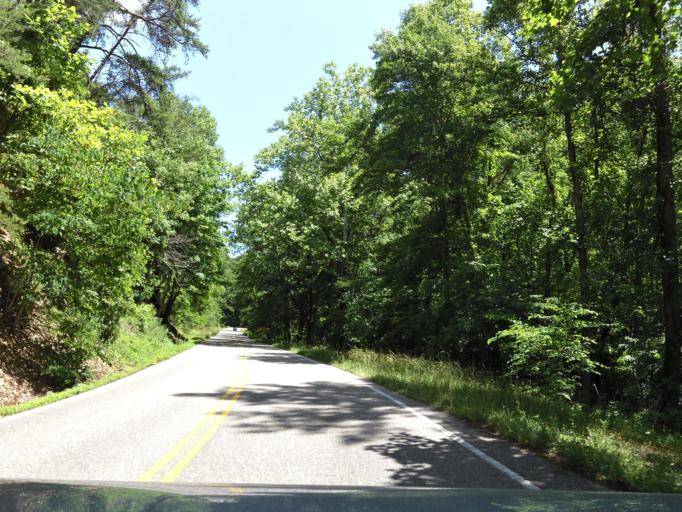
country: US
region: Tennessee
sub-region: Loudon County
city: Greenback
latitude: 35.5124
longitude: -83.9872
